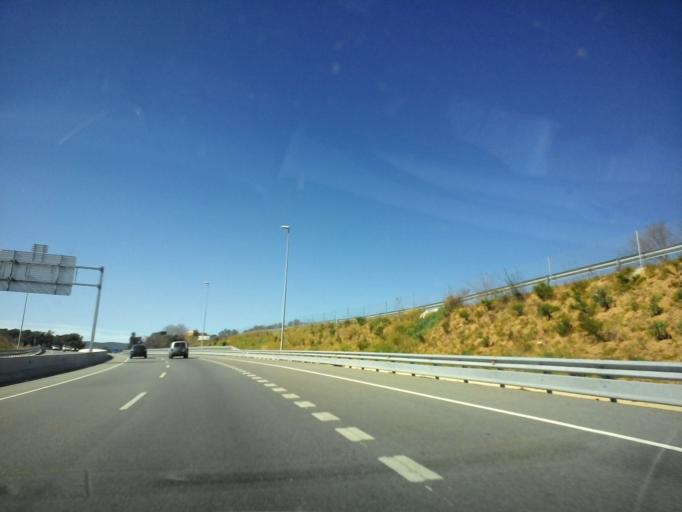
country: ES
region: Catalonia
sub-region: Provincia de Girona
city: Palamos
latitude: 41.8601
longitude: 3.1147
